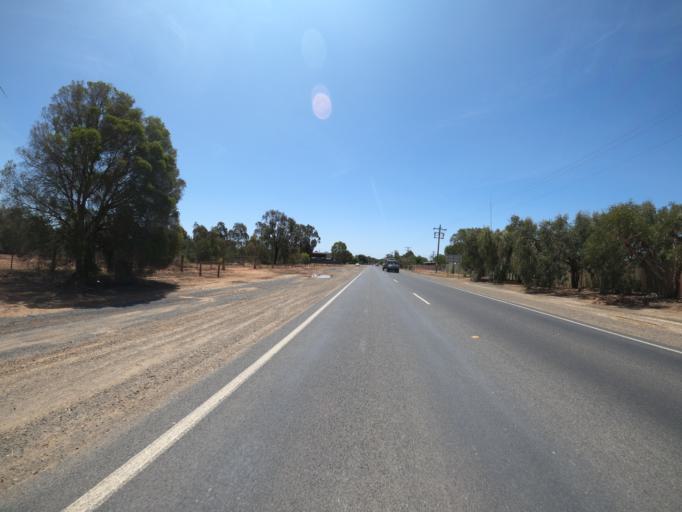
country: AU
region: Victoria
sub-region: Moira
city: Yarrawonga
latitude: -36.0226
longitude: 145.9955
